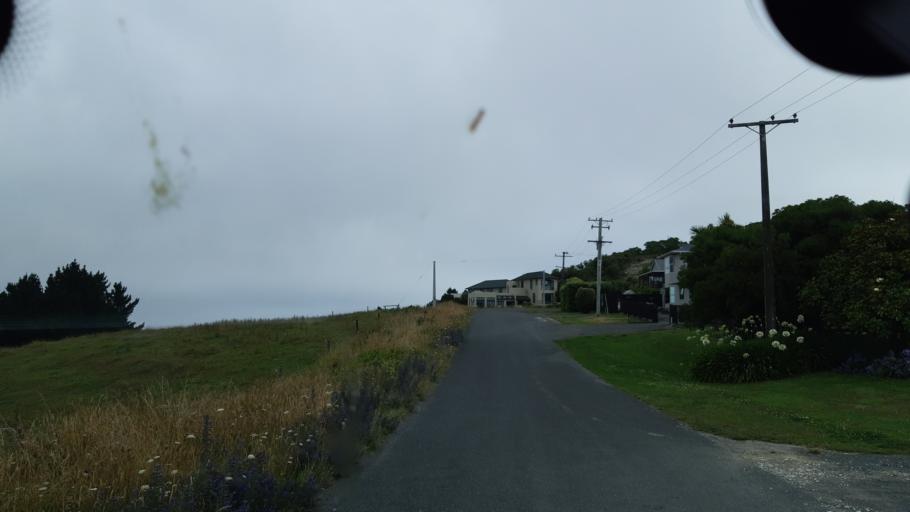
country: NZ
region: Canterbury
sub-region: Kaikoura District
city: Kaikoura
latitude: -42.4194
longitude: 173.6995
